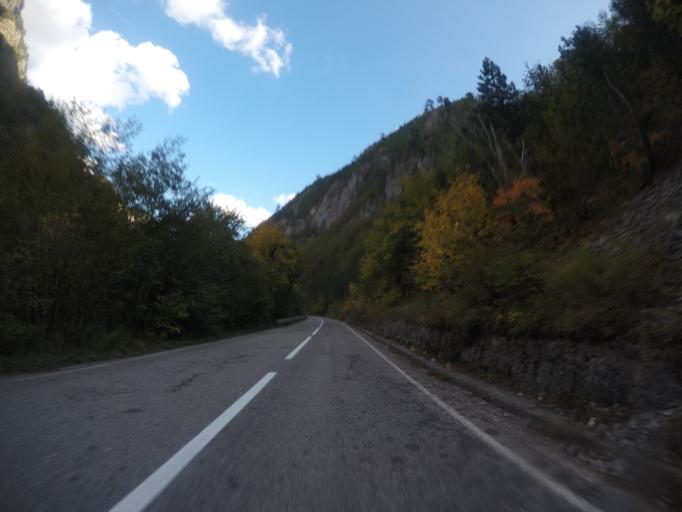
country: ME
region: Opstina Zabljak
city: Zabljak
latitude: 43.1250
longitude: 19.3289
